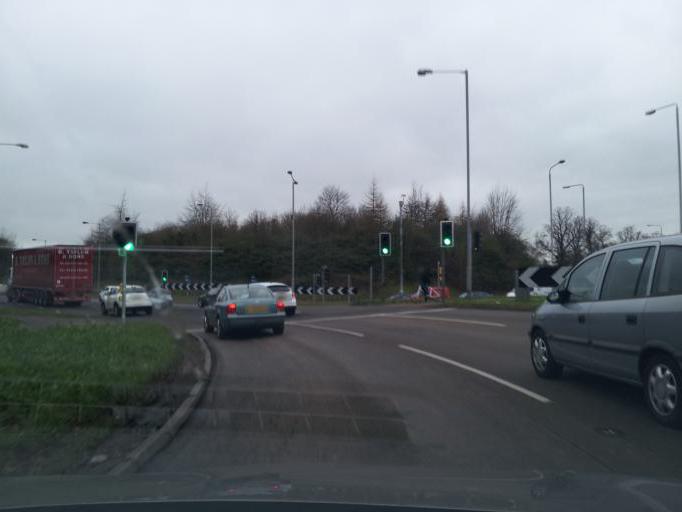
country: GB
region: England
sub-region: Nottinghamshire
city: Kimberley
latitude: 52.9903
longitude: -1.2217
